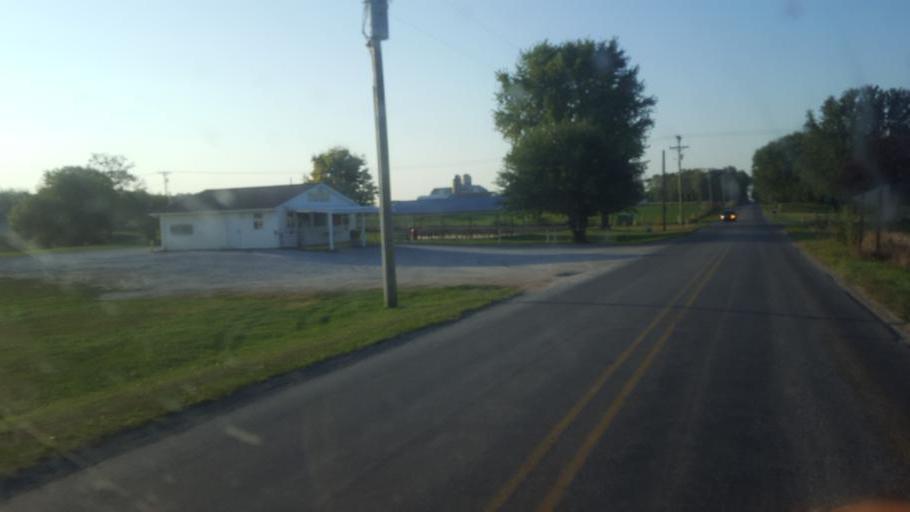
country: US
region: Indiana
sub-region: LaGrange County
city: Lagrange
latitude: 41.6278
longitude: -85.4247
